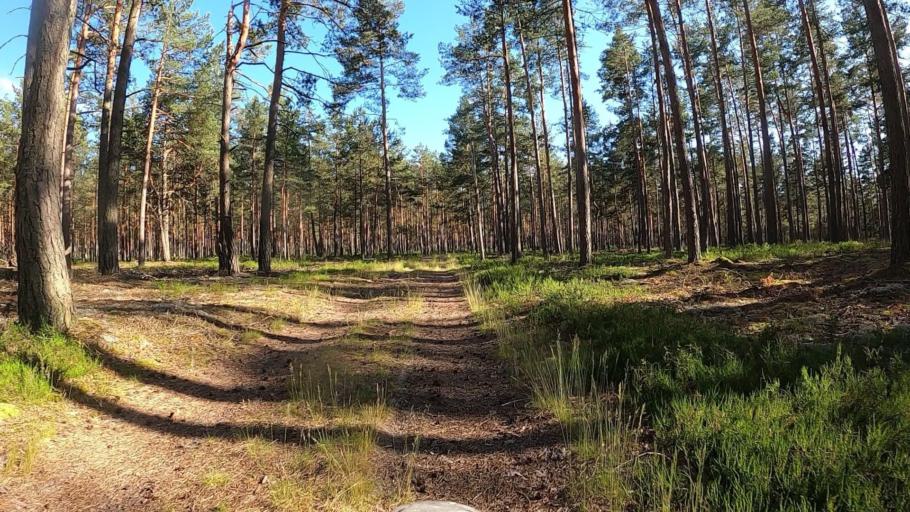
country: LV
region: Carnikava
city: Carnikava
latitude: 57.1067
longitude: 24.2419
